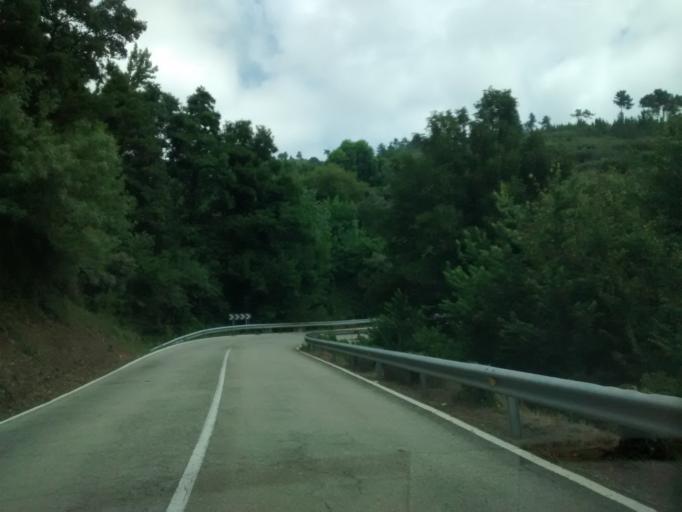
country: ES
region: Galicia
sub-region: Provincia de Ourense
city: Manzaneda
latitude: 42.3367
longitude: -7.1892
